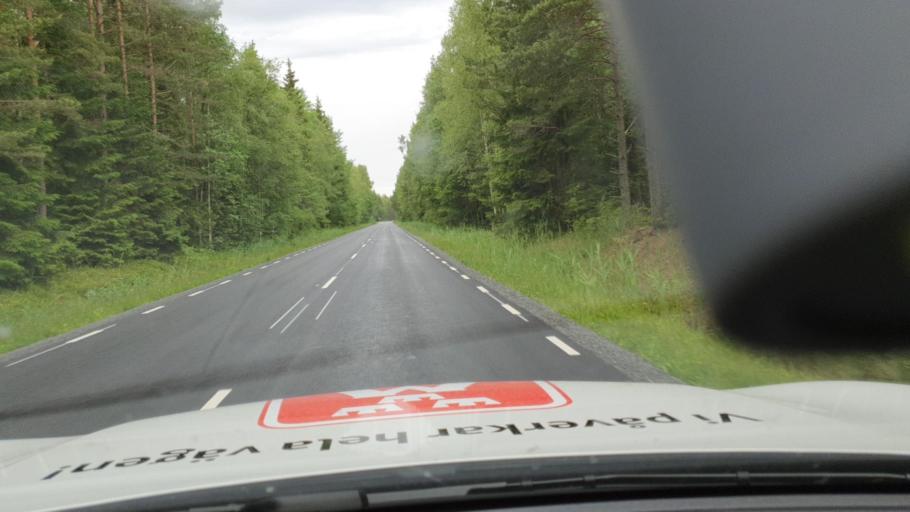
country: SE
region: Vaestra Goetaland
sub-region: Gullspangs Kommun
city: Anderstorp
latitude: 58.9226
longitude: 14.4288
